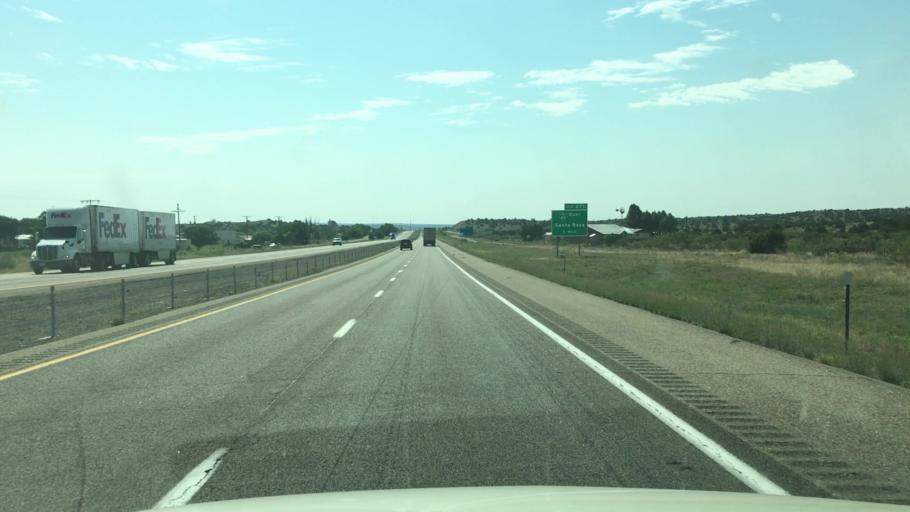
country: US
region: New Mexico
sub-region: Guadalupe County
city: Santa Rosa
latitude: 34.9569
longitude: -104.7274
